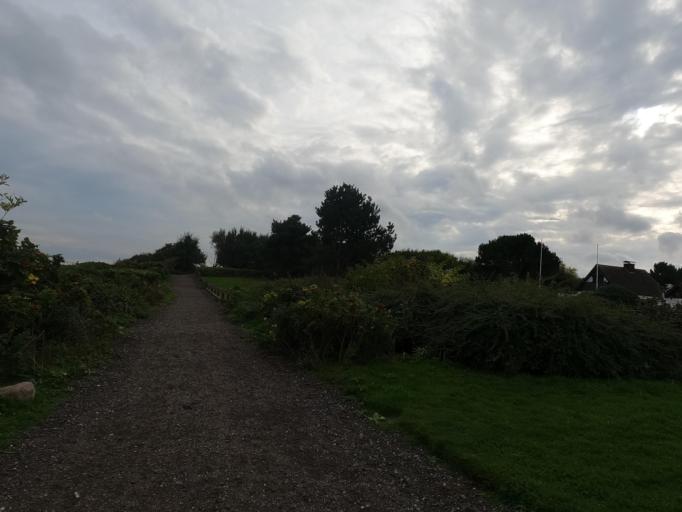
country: DE
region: Schleswig-Holstein
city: Grossenbrode
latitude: 54.3354
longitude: 11.0716
